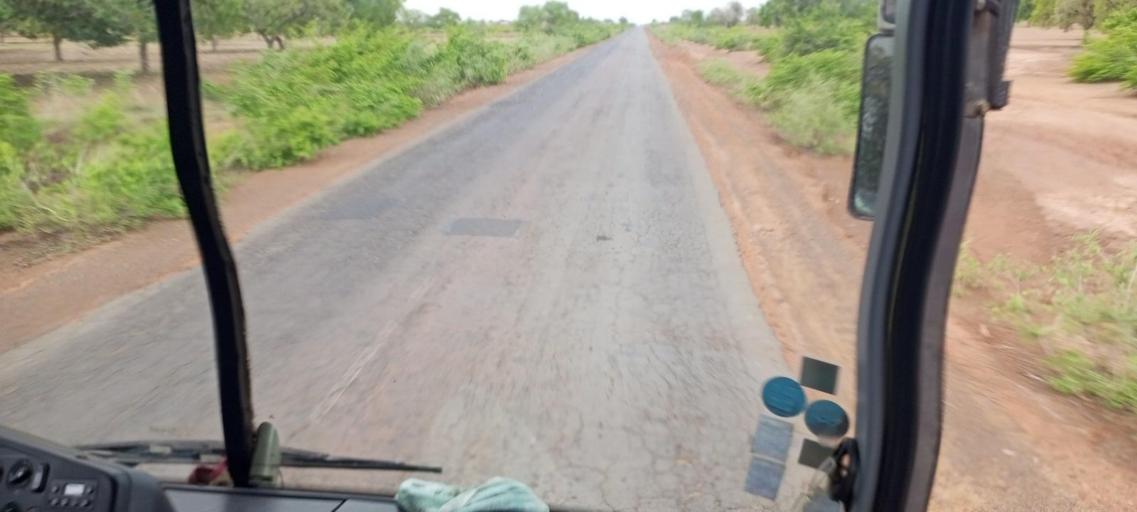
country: ML
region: Segou
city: Bla
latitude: 12.7251
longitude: -5.7252
